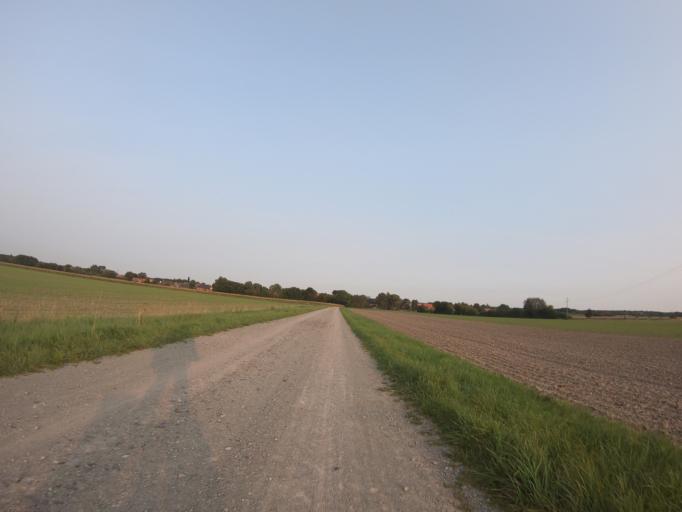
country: DE
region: Lower Saxony
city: Ribbesbuttel
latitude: 52.4268
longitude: 10.4762
